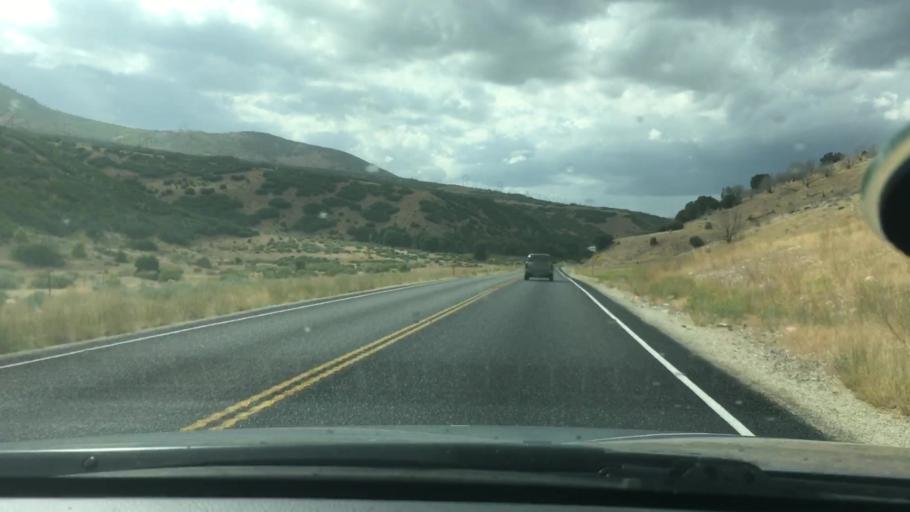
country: US
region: Utah
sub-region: Sanpete County
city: Fountain Green
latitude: 39.7026
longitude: -111.7033
